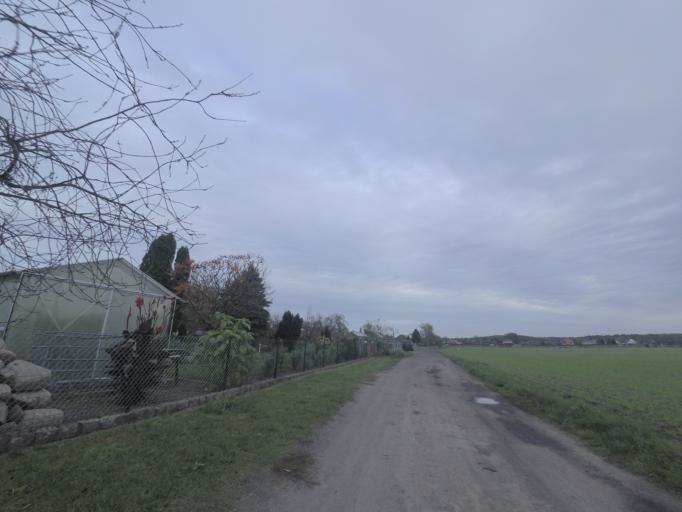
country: DE
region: Brandenburg
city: Rangsdorf
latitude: 52.2717
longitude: 13.3455
